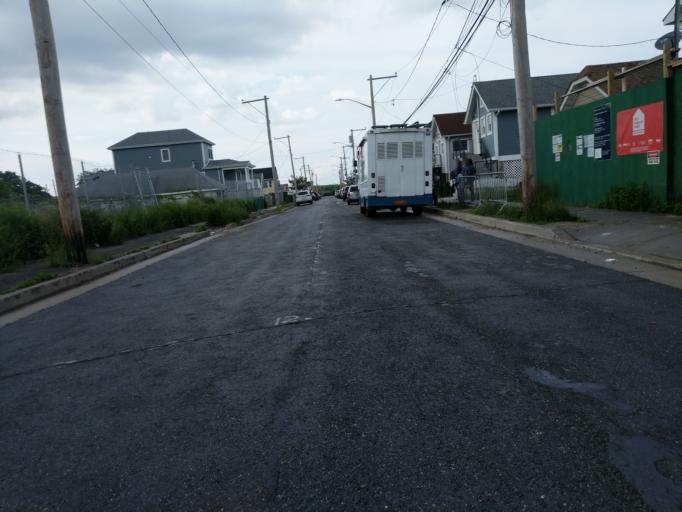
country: US
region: New York
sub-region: Nassau County
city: Inwood
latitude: 40.5968
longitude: -73.7767
